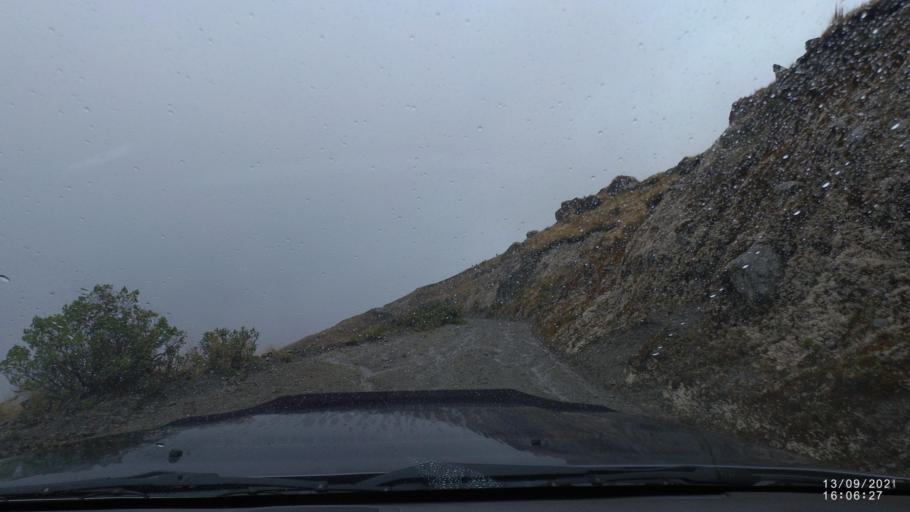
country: BO
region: Cochabamba
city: Colomi
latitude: -17.2821
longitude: -65.7105
